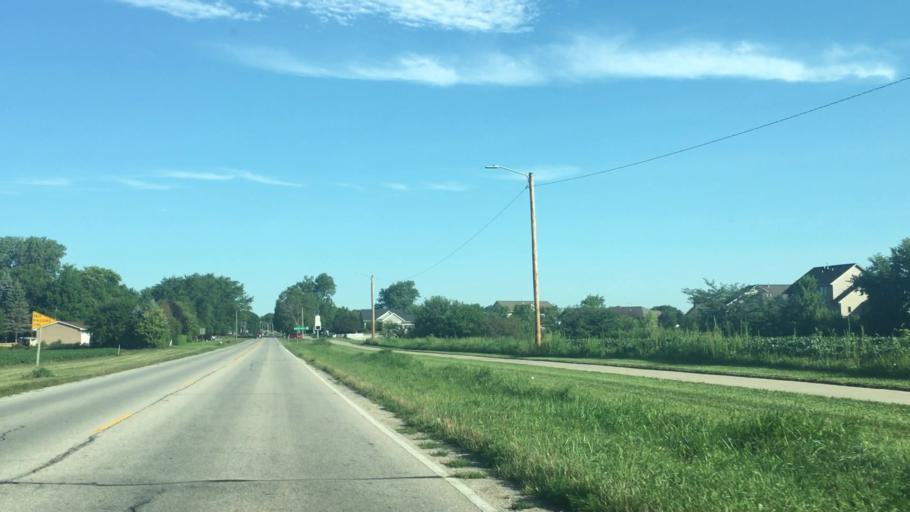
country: US
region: Iowa
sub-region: Johnson County
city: North Liberty
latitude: 41.7402
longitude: -91.5873
